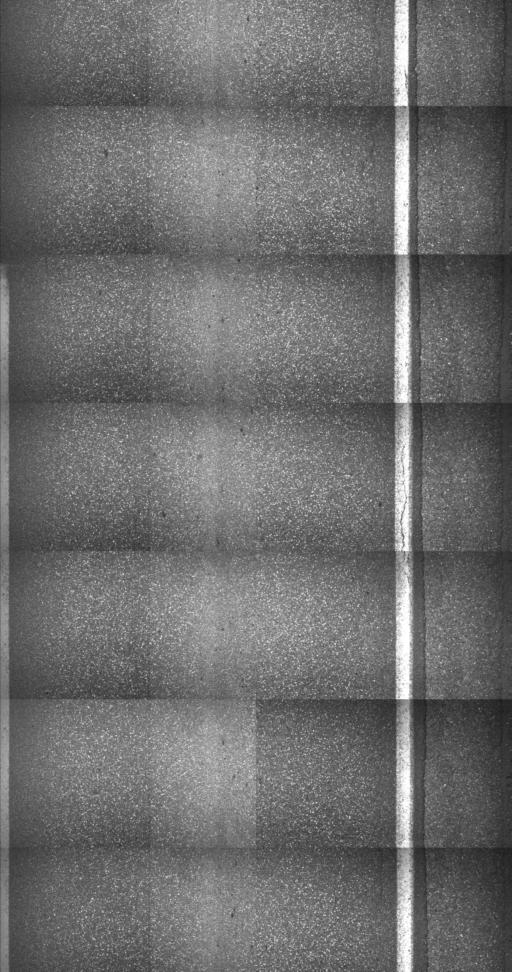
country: US
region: Vermont
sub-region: Caledonia County
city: Hardwick
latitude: 44.5241
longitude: -72.4184
